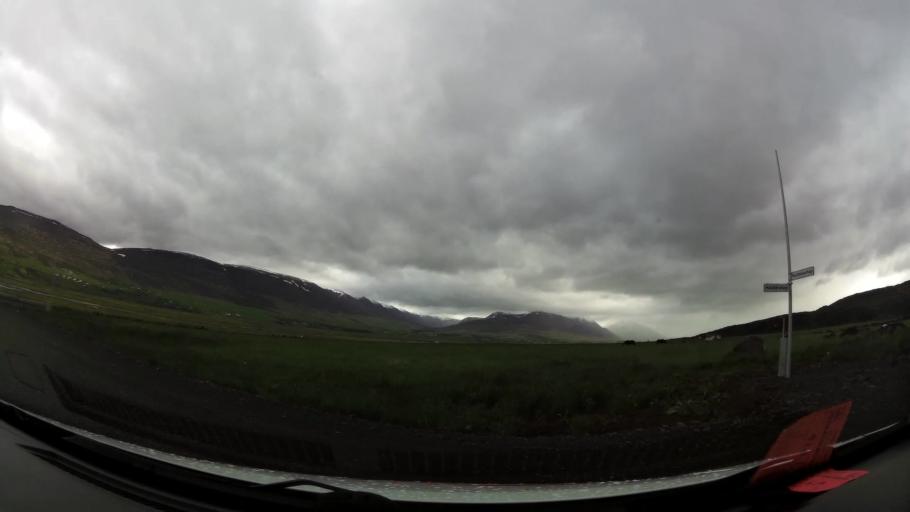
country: IS
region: Northeast
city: Akureyri
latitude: 65.6583
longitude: -18.0919
